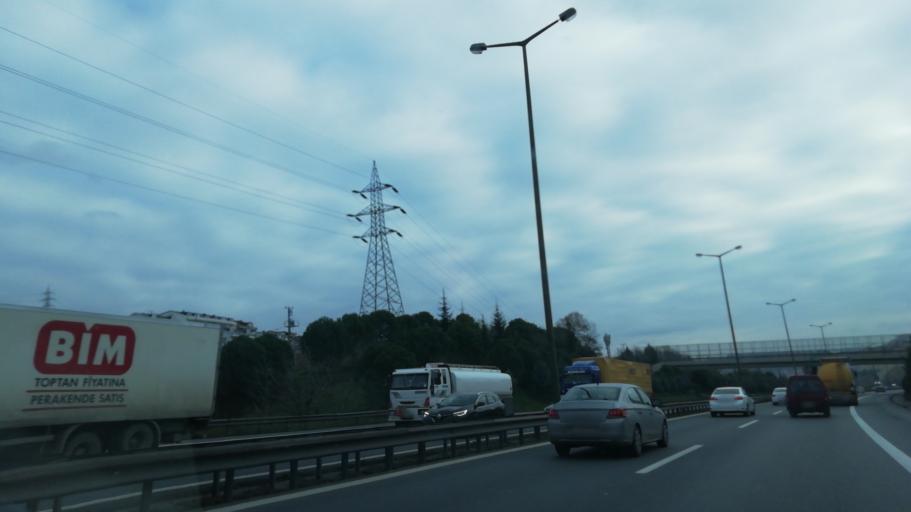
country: TR
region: Kocaeli
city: Izmit
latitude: 40.7859
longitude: 29.9526
